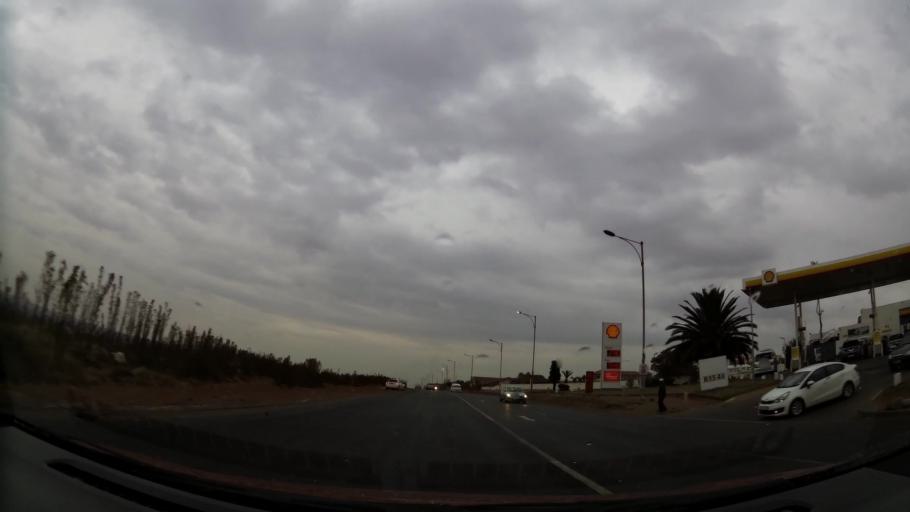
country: ZA
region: Gauteng
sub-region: City of Johannesburg Metropolitan Municipality
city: Roodepoort
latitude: -26.1646
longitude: 27.8062
